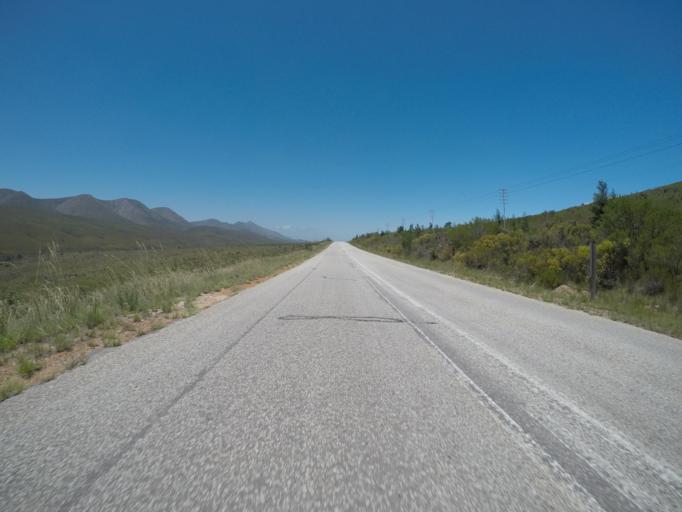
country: ZA
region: Eastern Cape
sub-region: Cacadu District Municipality
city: Kareedouw
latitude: -33.8871
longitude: 24.0871
